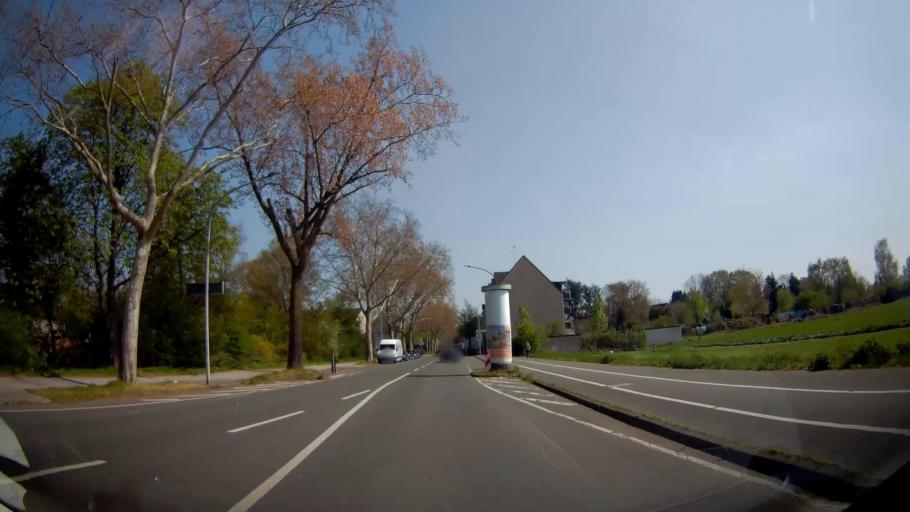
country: DE
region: North Rhine-Westphalia
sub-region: Regierungsbezirk Munster
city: Gelsenkirchen
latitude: 51.5322
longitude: 7.1160
